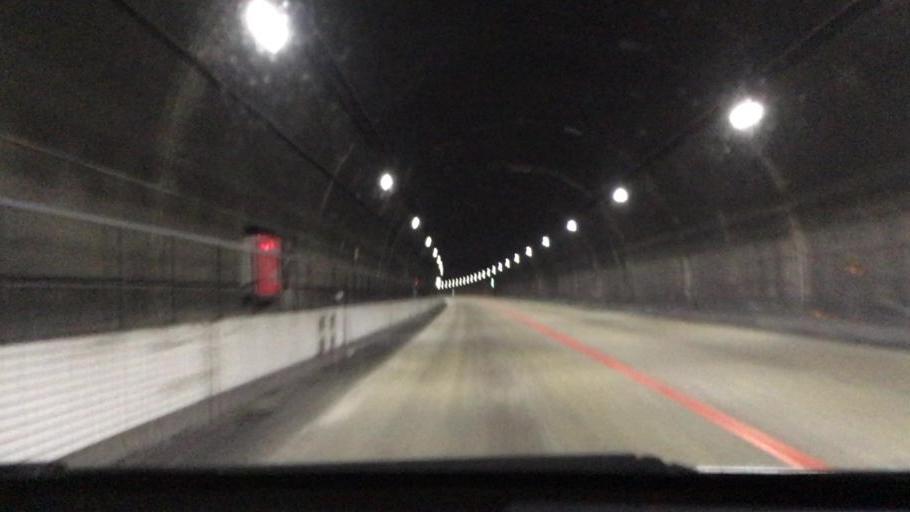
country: JP
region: Yamaguchi
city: Tokuyama
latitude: 34.0704
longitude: 131.8255
